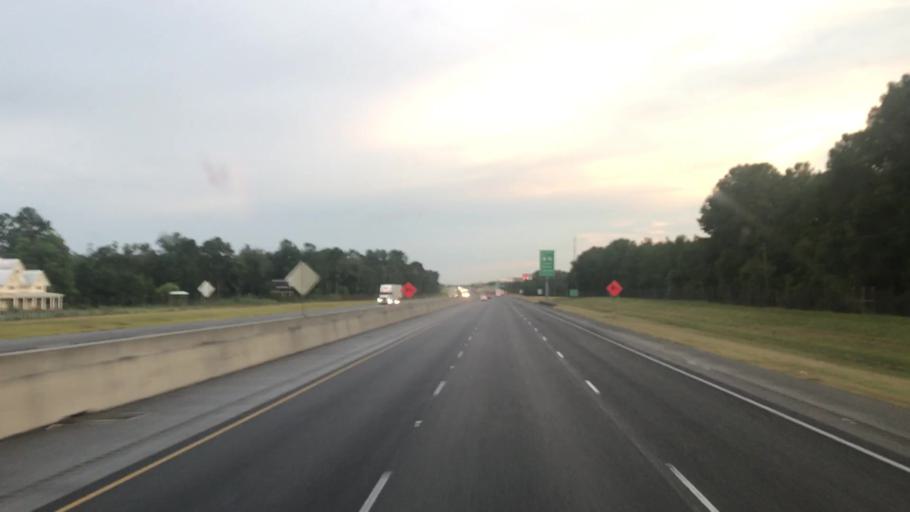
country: US
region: Georgia
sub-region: Lowndes County
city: Hahira
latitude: 31.0103
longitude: -83.3934
